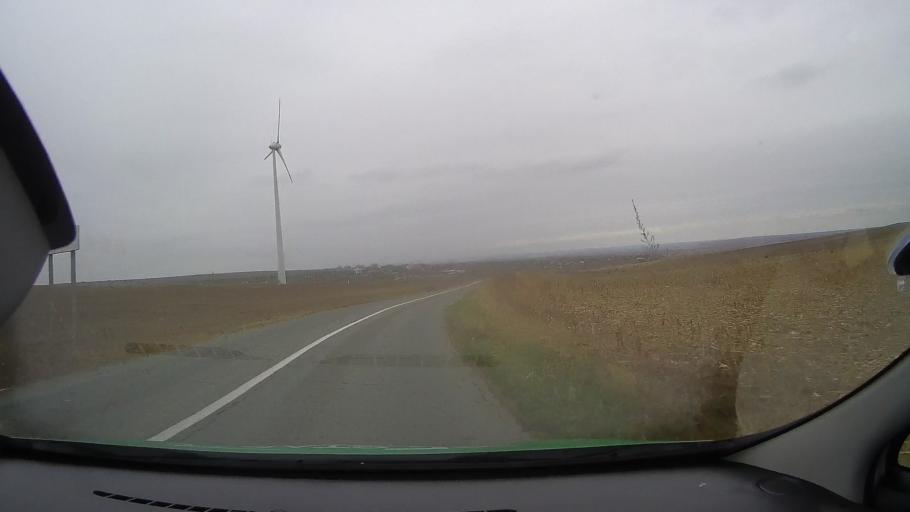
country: RO
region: Constanta
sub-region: Comuna Pantelimon
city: Pantelimon
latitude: 44.5344
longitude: 28.3262
